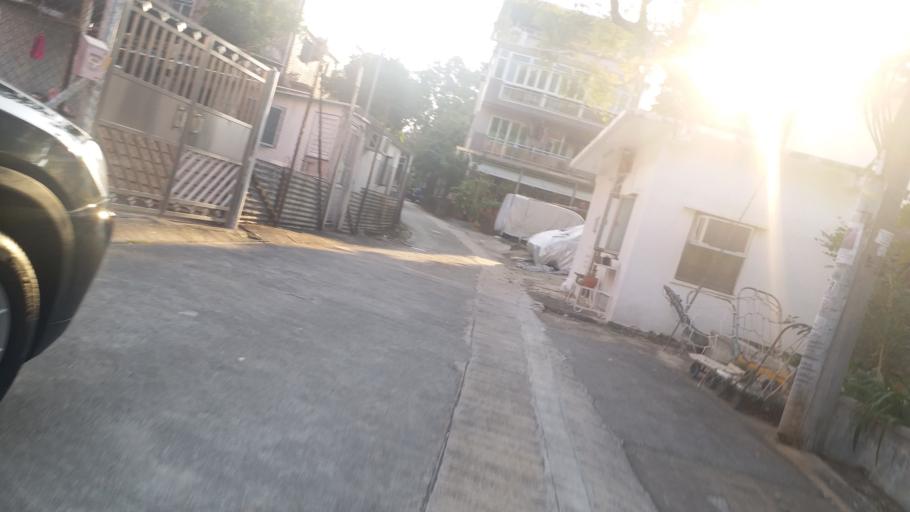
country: HK
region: Tuen Mun
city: Tuen Mun
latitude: 22.4124
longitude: 113.9748
